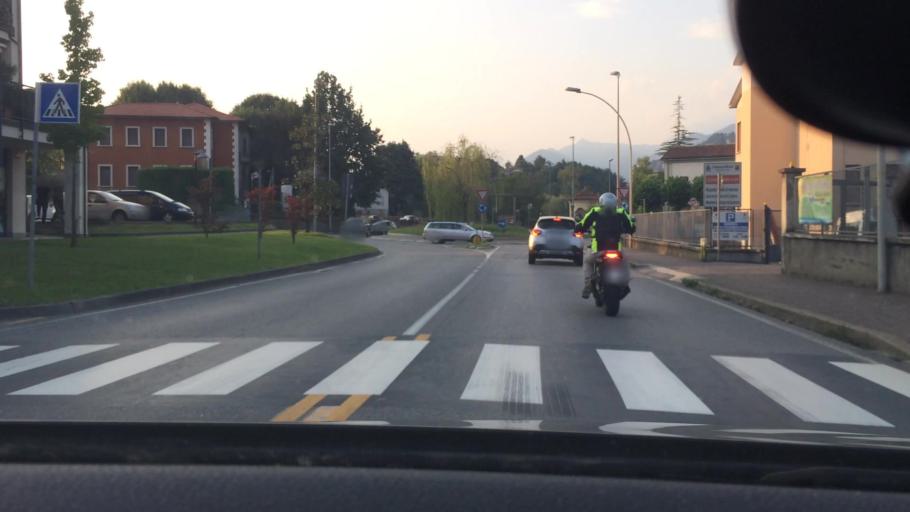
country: IT
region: Lombardy
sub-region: Provincia di Lecco
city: Brivio
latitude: 45.7415
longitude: 9.4458
